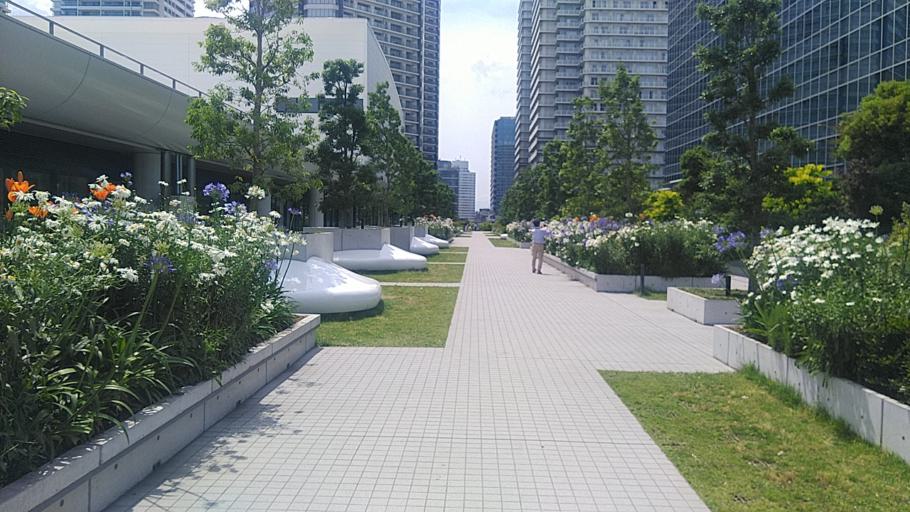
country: JP
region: Kanagawa
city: Yokohama
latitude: 35.4621
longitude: 139.6346
